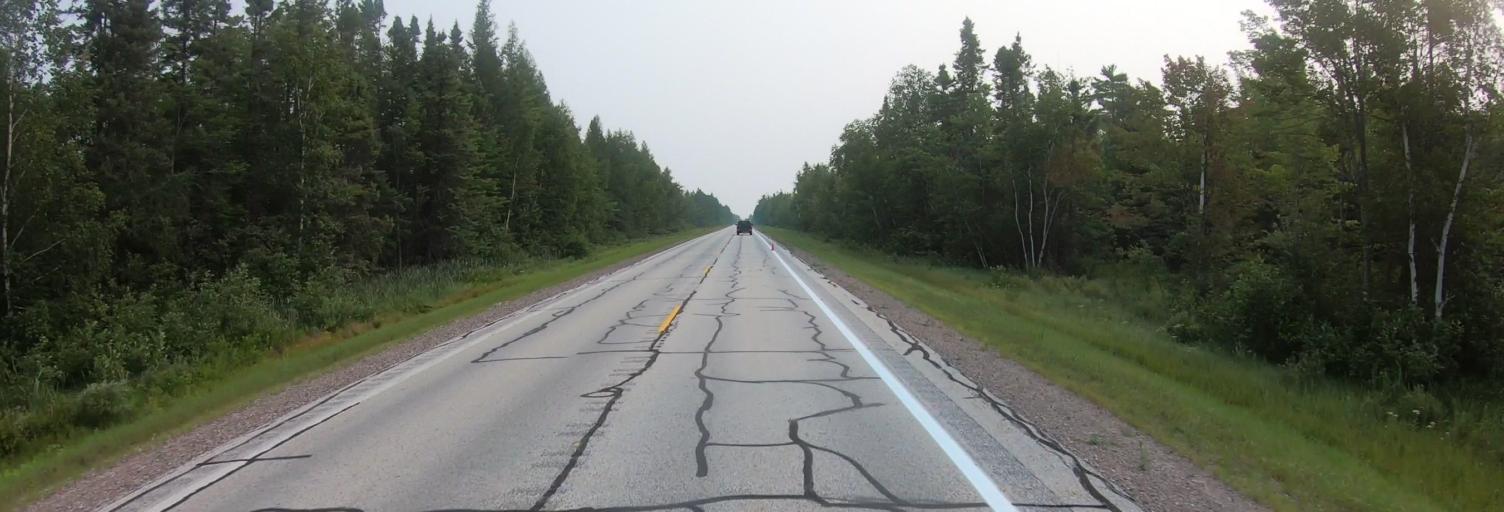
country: US
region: Michigan
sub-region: Luce County
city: Newberry
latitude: 46.5445
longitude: -85.0446
